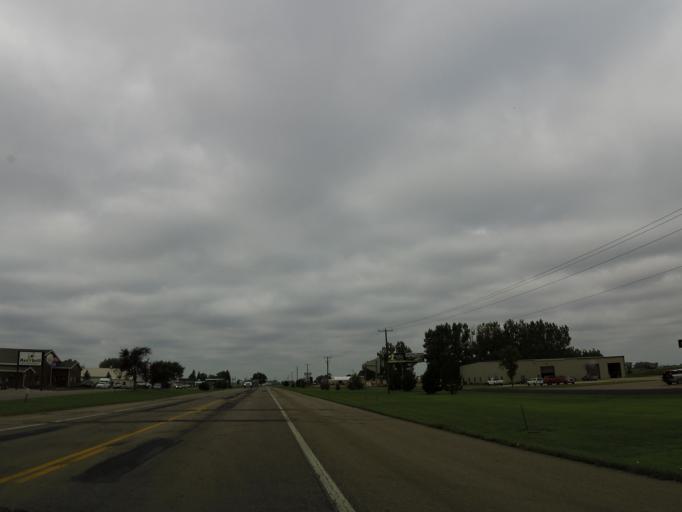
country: US
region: Minnesota
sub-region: Renville County
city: Olivia
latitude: 44.7778
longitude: -95.0200
